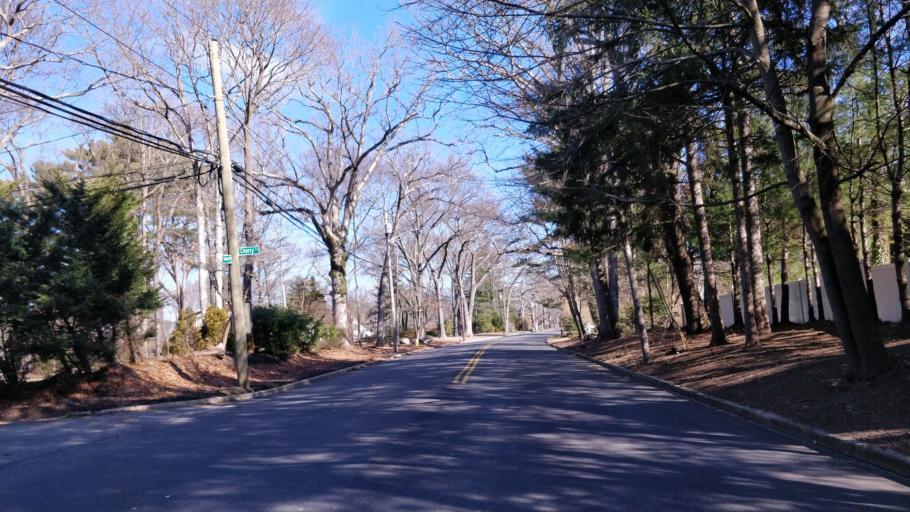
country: US
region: New York
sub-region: Suffolk County
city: Smithtown
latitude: 40.8582
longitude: -73.2023
